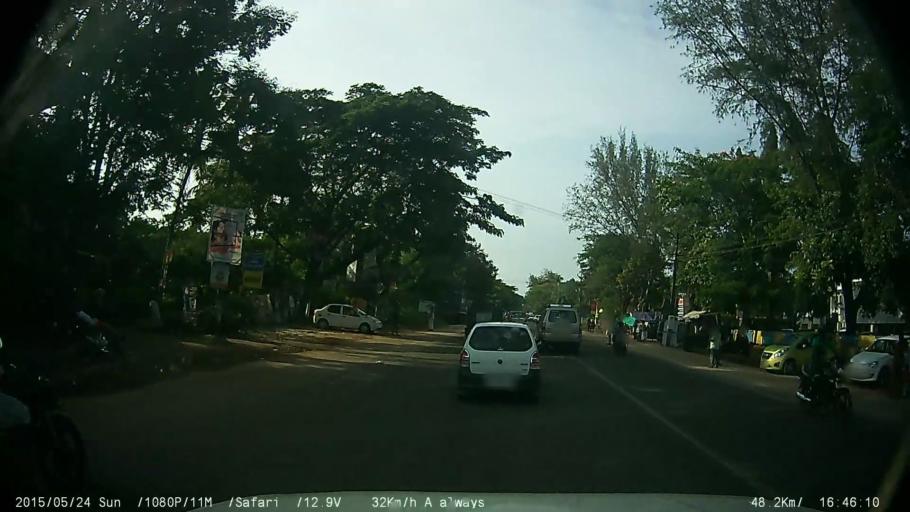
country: IN
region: Kerala
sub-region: Alappuzha
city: Shertallai
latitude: 9.6668
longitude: 76.3391
